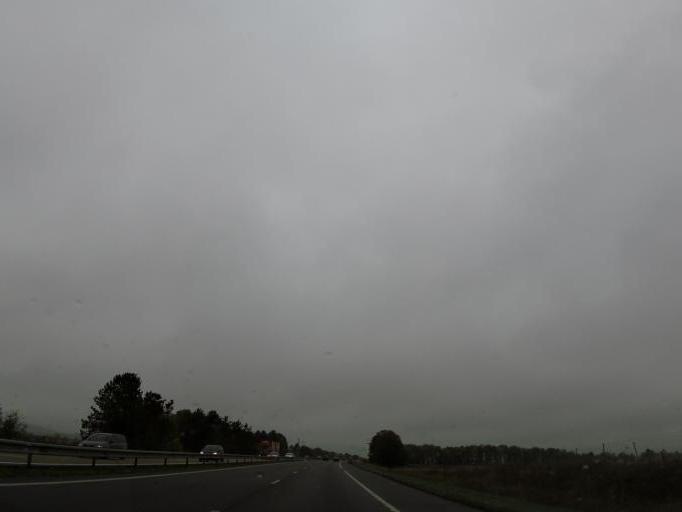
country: FR
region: Champagne-Ardenne
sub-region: Departement de la Marne
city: Verzy
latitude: 49.0940
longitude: 4.2566
